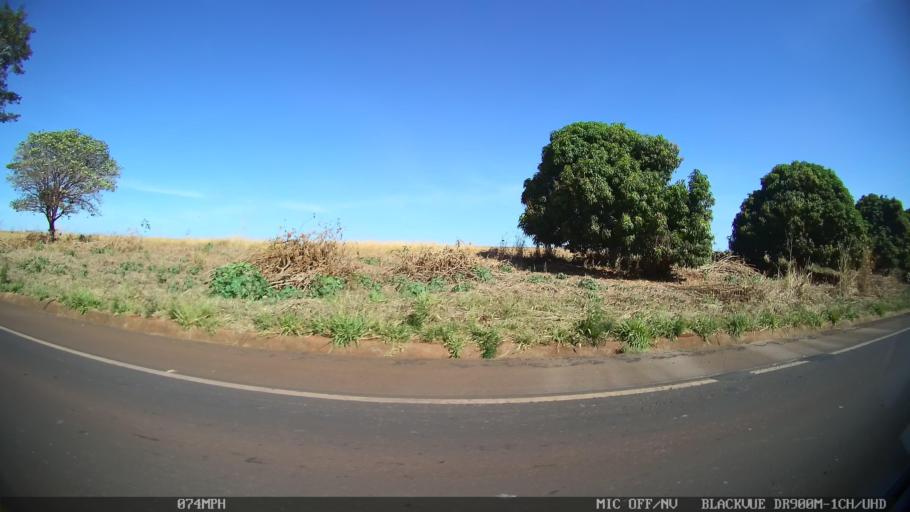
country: BR
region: Sao Paulo
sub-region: Ipua
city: Ipua
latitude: -20.4822
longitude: -48.0759
